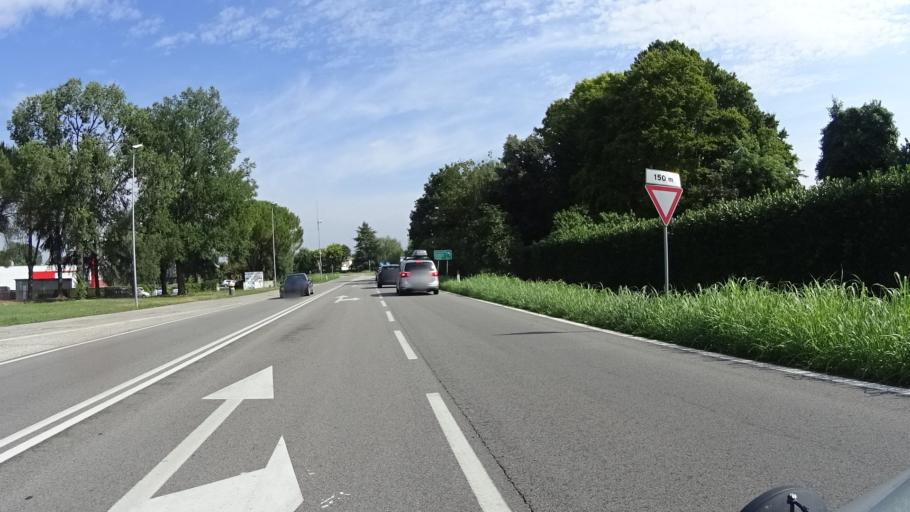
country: IT
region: Veneto
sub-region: Provincia di Venezia
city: San Michele al Tagliamento
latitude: 45.7685
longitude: 12.9848
